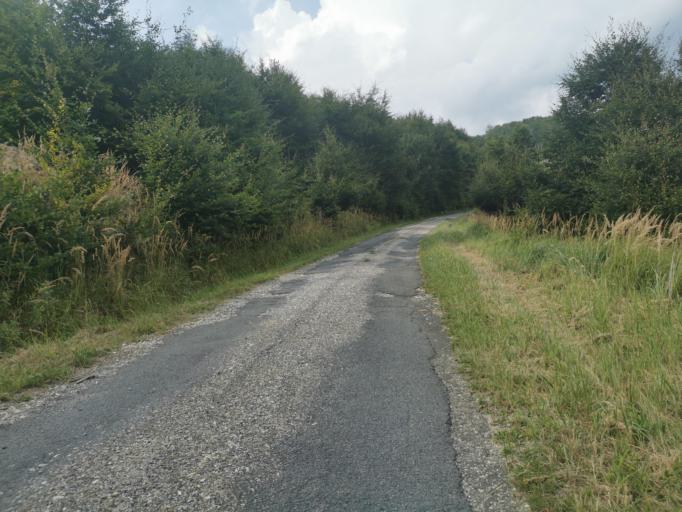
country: SK
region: Nitriansky
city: Stara Tura
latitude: 48.8325
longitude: 17.6235
